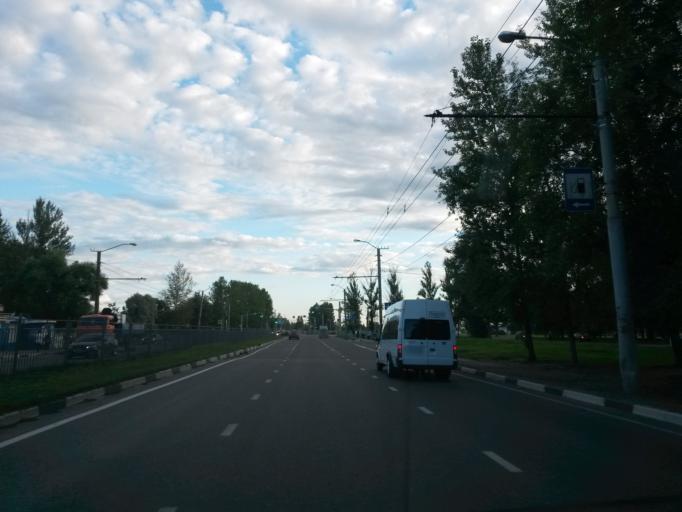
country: RU
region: Jaroslavl
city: Yaroslavl
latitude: 57.6760
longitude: 39.7749
